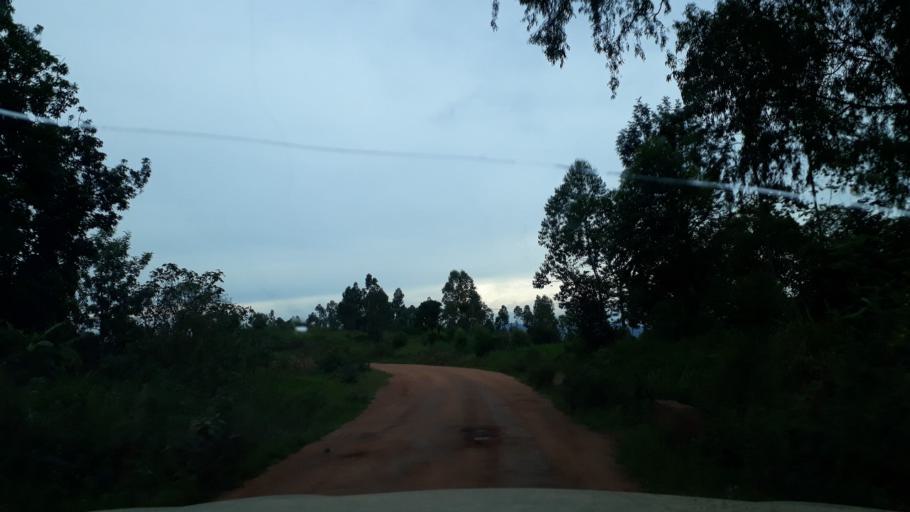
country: UG
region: Northern Region
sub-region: Zombo District
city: Paidha
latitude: 2.2178
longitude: 30.7782
